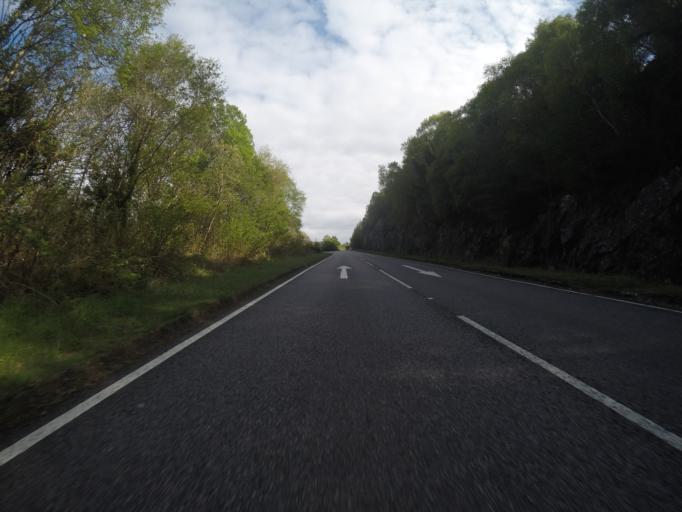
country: GB
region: Scotland
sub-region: Highland
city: Portree
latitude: 57.2616
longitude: -5.9461
